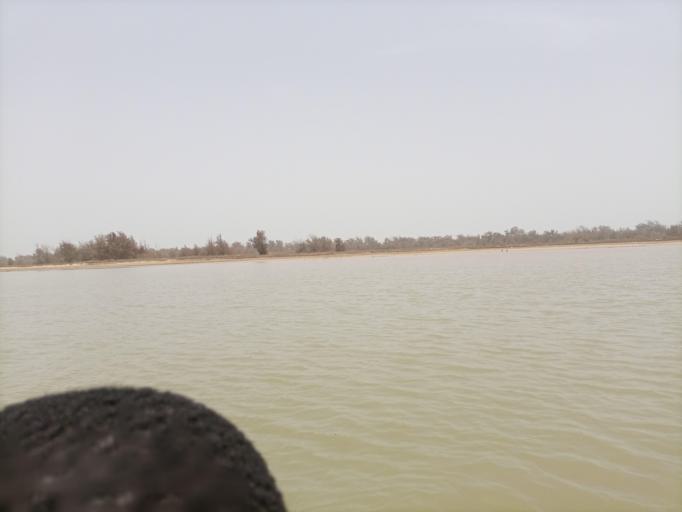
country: SN
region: Saint-Louis
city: Saint-Louis
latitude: 15.8538
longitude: -16.5174
